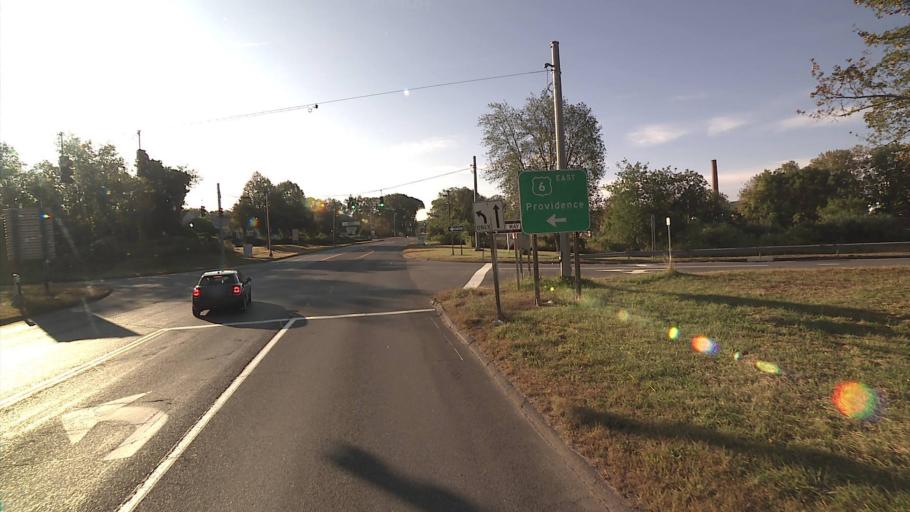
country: US
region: Connecticut
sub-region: Windham County
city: Willimantic
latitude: 41.7257
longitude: -72.2421
